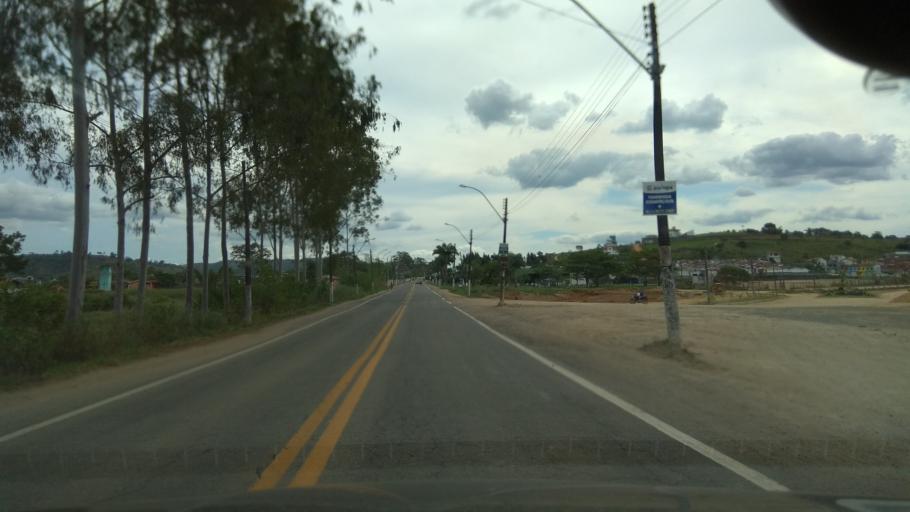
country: BR
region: Bahia
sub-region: Ipiau
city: Ipiau
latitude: -14.1425
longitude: -39.7218
